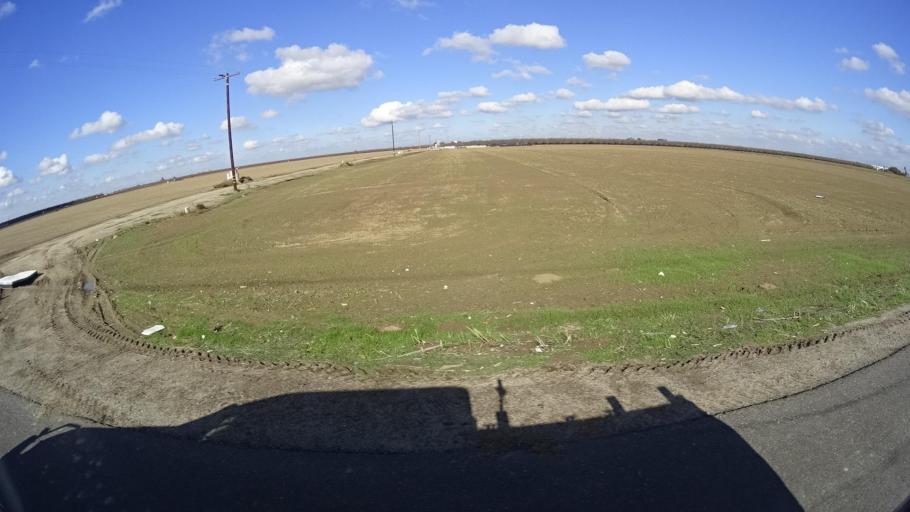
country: US
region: California
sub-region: Kern County
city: McFarland
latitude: 35.7179
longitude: -119.2491
